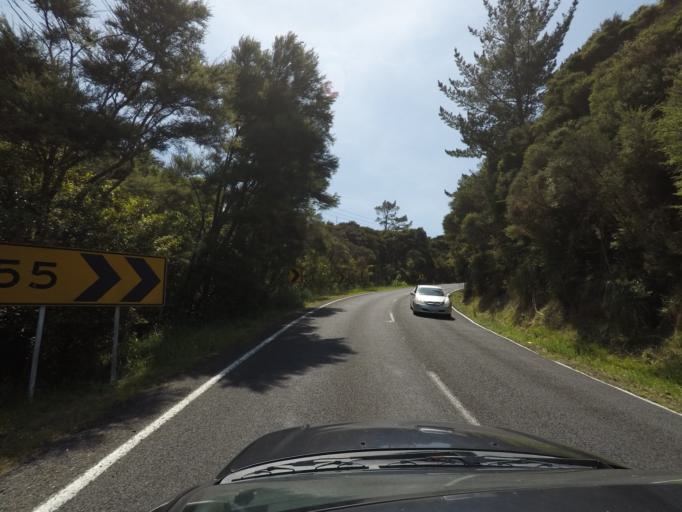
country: NZ
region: Auckland
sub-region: Auckland
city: Titirangi
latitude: -36.9856
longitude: 174.6057
